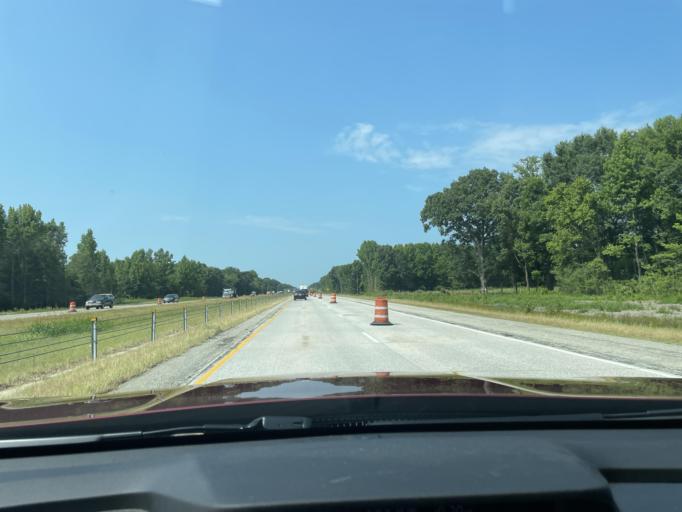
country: US
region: Arkansas
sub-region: White County
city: Searcy
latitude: 35.1813
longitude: -91.7581
